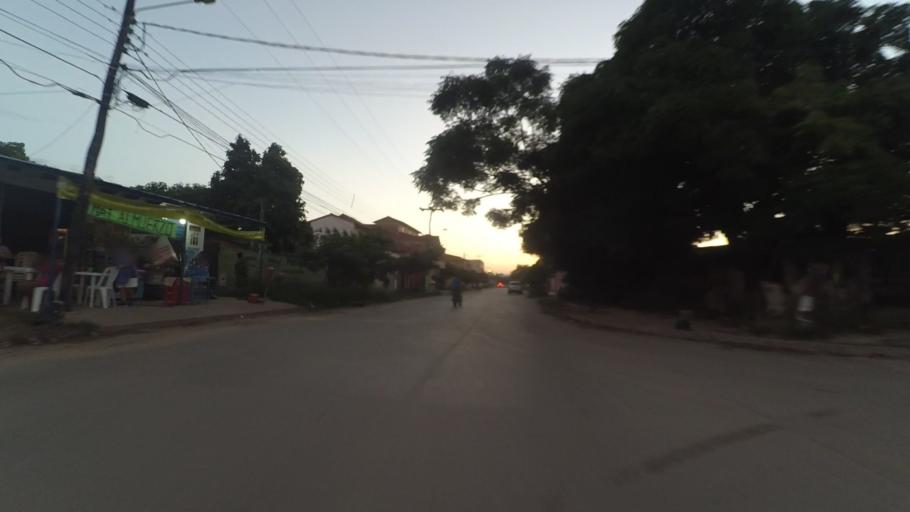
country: BO
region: Santa Cruz
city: Santa Cruz de la Sierra
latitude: -17.8211
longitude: -63.1335
